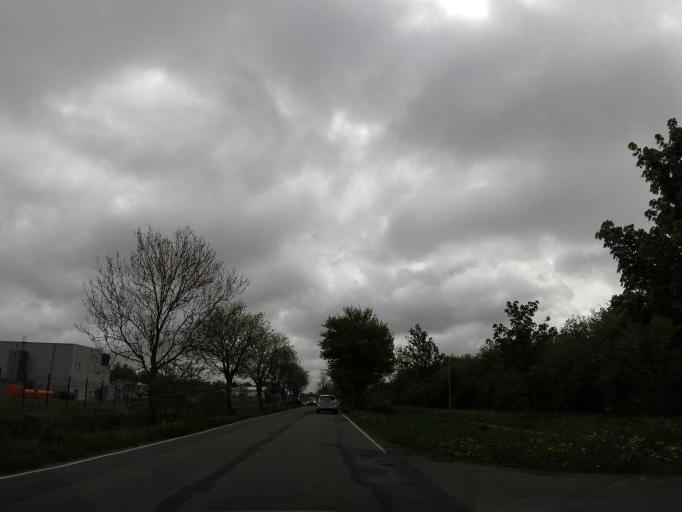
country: DE
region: Schleswig-Holstein
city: Niebull
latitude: 54.7807
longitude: 8.8313
